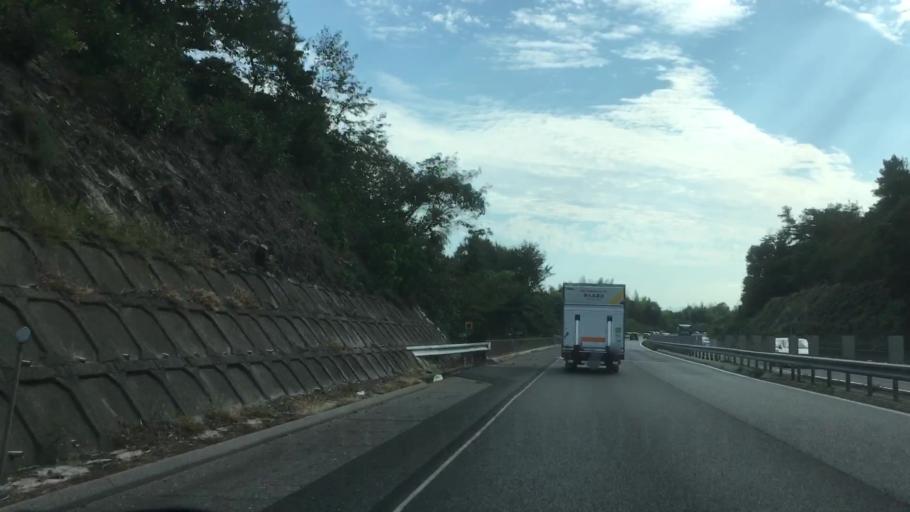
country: JP
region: Hiroshima
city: Ono-hara
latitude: 34.3097
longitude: 132.2802
